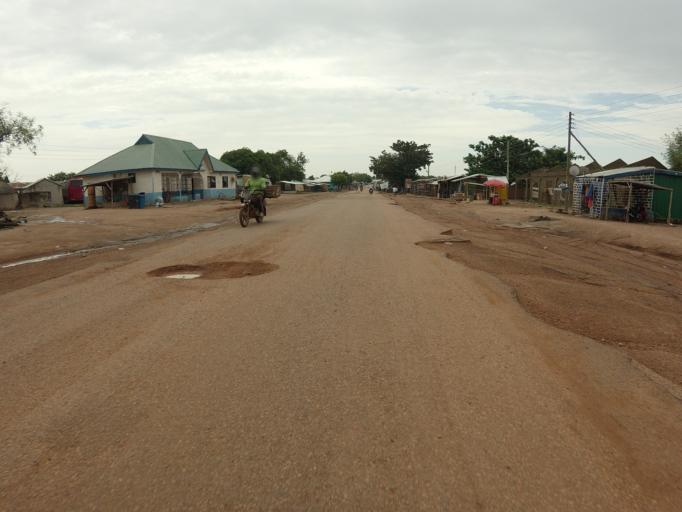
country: GH
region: Upper East
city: Bawku
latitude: 10.9377
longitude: -0.4891
